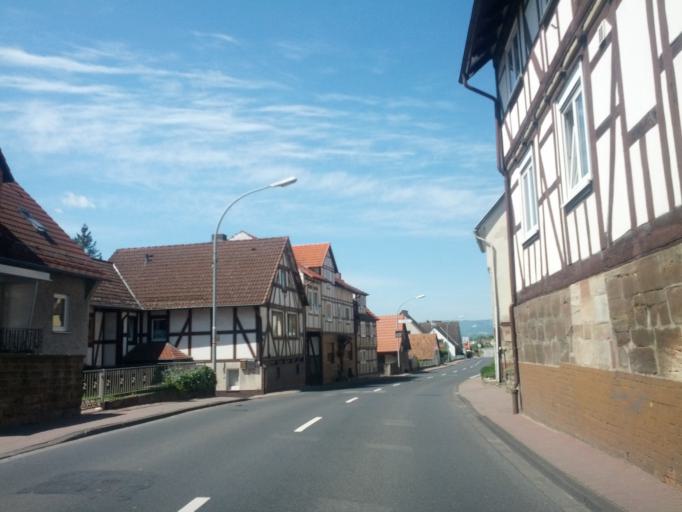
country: DE
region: Hesse
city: Wanfried
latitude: 51.1902
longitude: 10.1261
